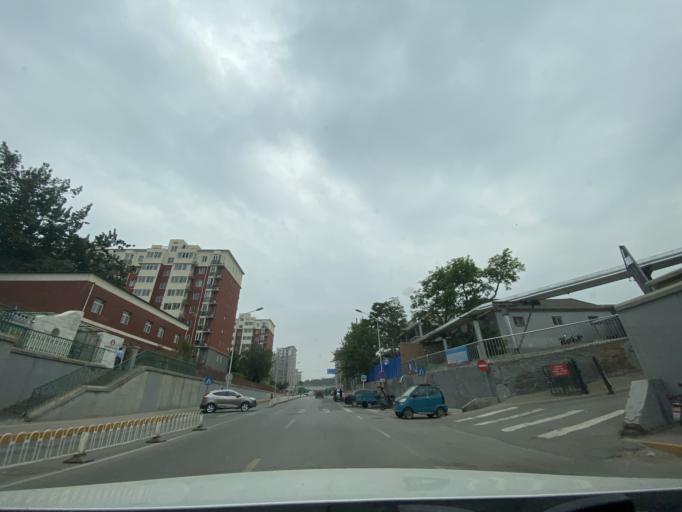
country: CN
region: Beijing
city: Sijiqing
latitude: 39.9303
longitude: 116.2421
